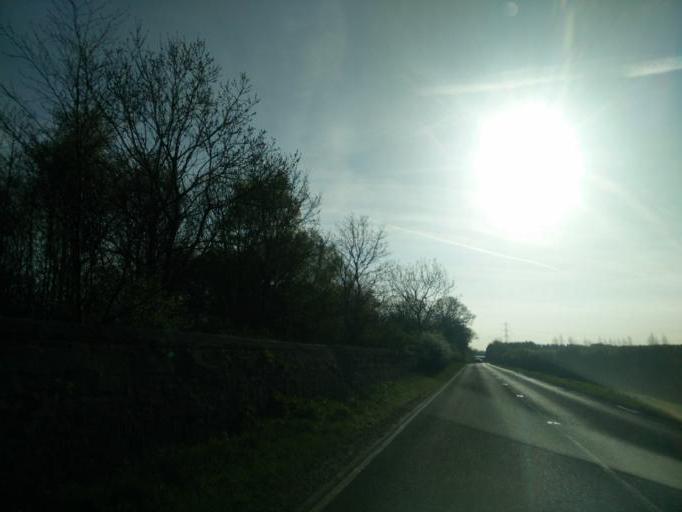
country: GB
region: England
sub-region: Stockton-on-Tees
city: Grindon
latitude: 54.6202
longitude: -1.3349
